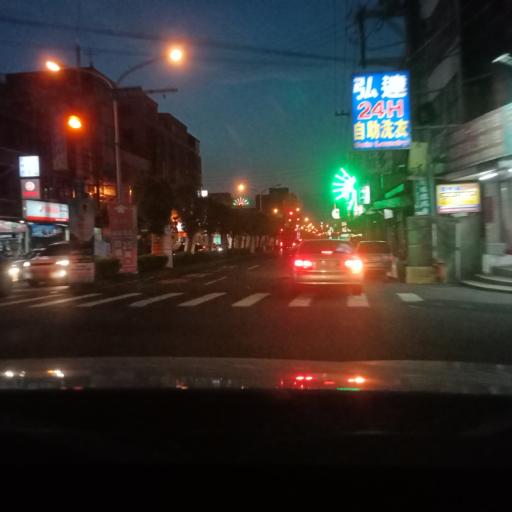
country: TW
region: Taiwan
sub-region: Hsinchu
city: Zhubei
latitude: 24.9021
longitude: 121.0489
